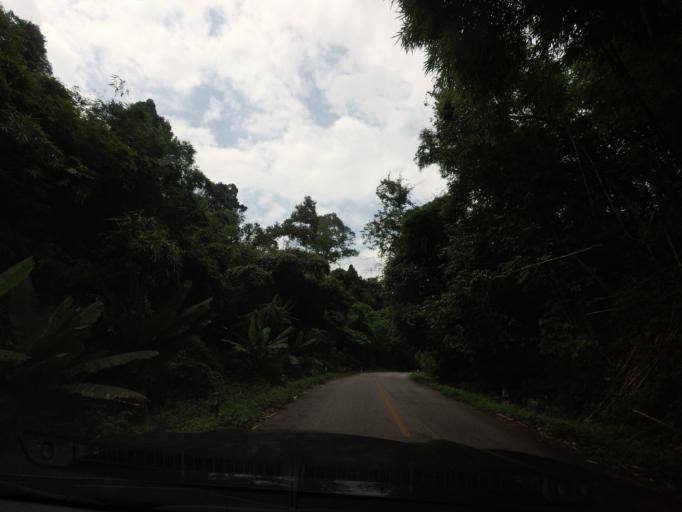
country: TH
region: Loei
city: Na Haeo
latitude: 17.7168
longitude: 100.9474
